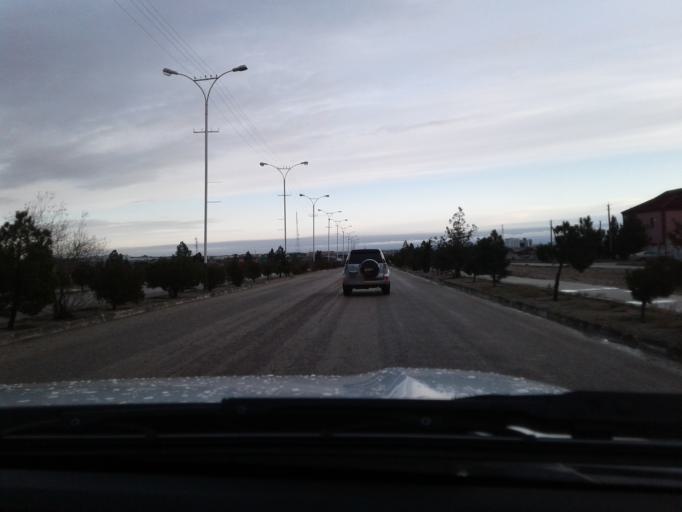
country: TM
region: Balkan
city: Balkanabat
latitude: 39.5354
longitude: 54.3521
